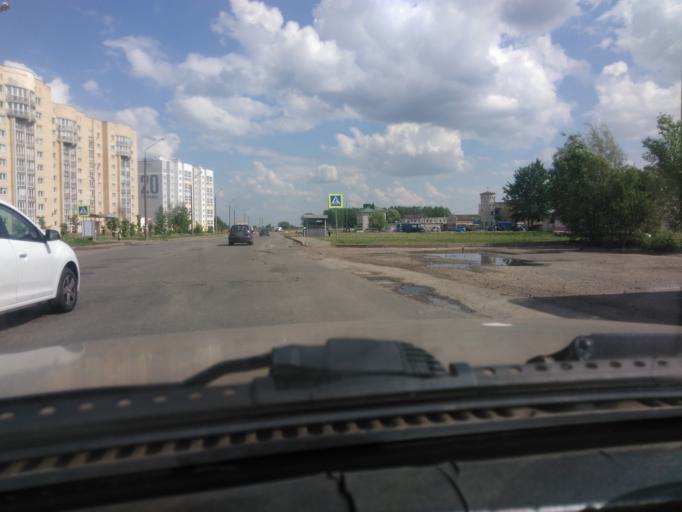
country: BY
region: Mogilev
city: Mahilyow
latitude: 53.9451
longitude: 30.3634
